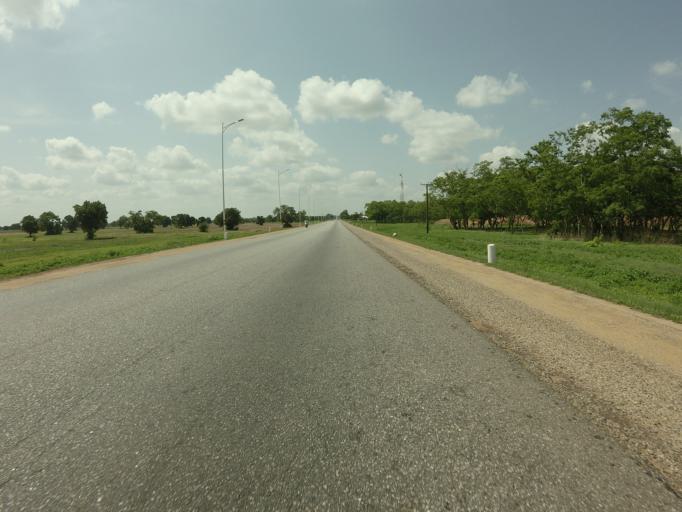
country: GH
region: Northern
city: Savelugu
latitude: 9.5423
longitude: -0.8388
